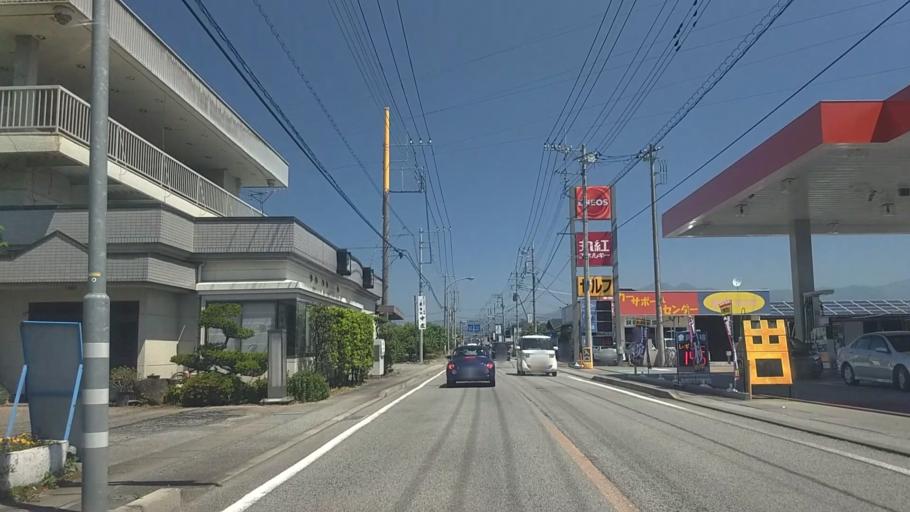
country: JP
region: Yamanashi
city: Ryuo
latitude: 35.6599
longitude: 138.4650
